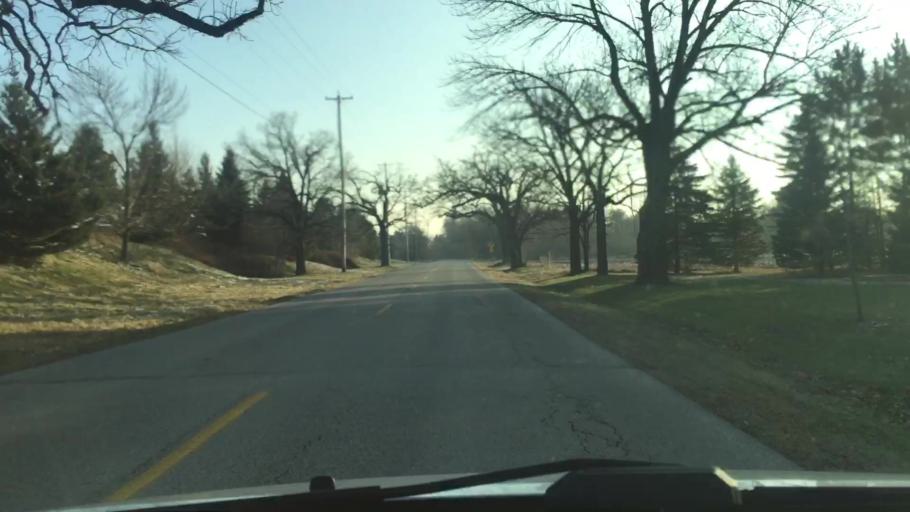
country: US
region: Wisconsin
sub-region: Waukesha County
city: Dousman
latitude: 43.0601
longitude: -88.4815
